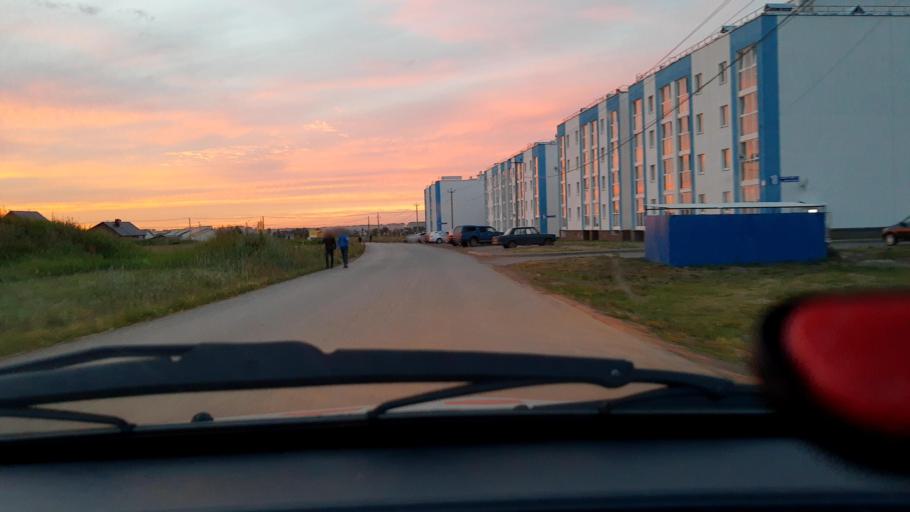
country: RU
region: Bashkortostan
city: Avdon
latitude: 54.4841
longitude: 55.8805
